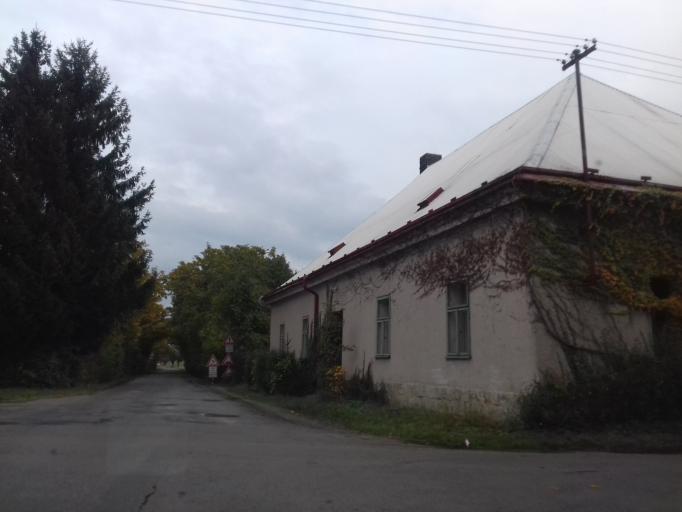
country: CZ
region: Pardubicky
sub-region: Okres Chrudim
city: Slatinany
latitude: 49.9326
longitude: 15.8509
